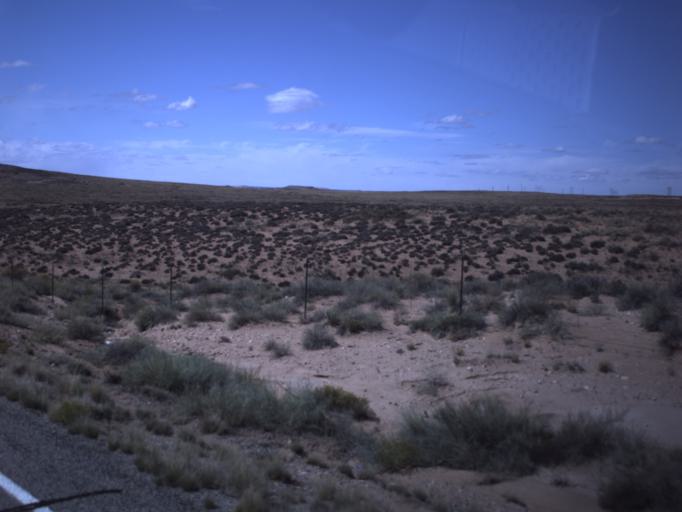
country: US
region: Utah
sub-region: San Juan County
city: Blanding
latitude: 37.2954
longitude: -109.4827
